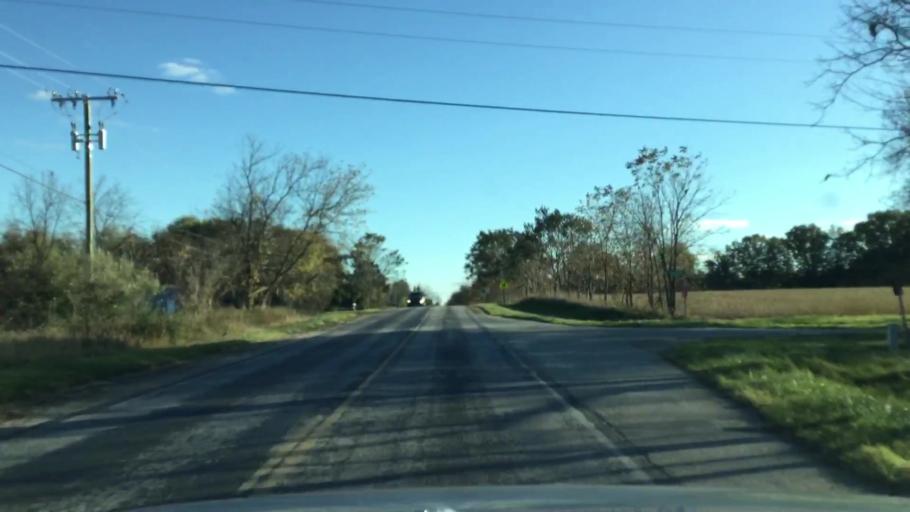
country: US
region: Michigan
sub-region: Lapeer County
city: Imlay City
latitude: 43.0557
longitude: -83.1680
